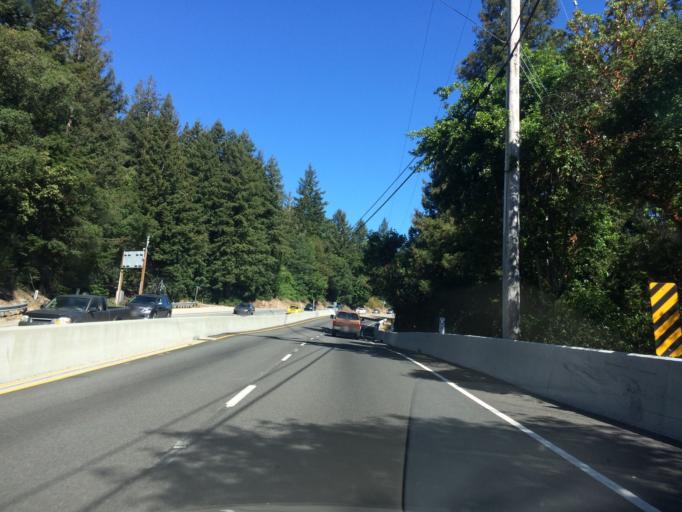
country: US
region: California
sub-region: Santa Clara County
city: Lexington Hills
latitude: 37.1266
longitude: -121.9742
